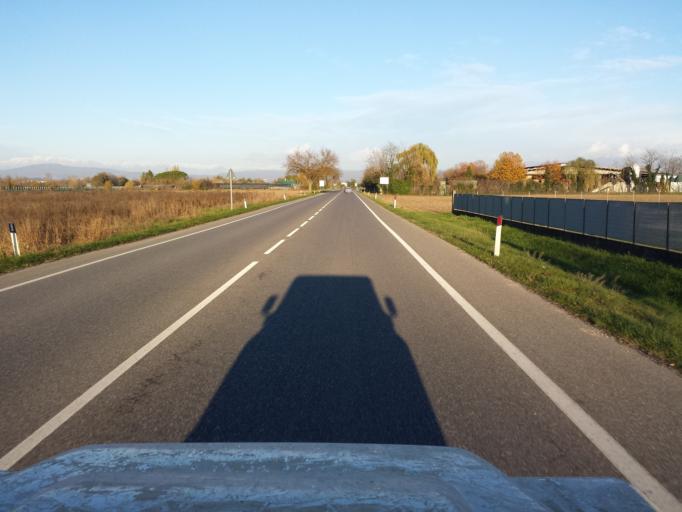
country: IT
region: Friuli Venezia Giulia
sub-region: Provincia di Gorizia
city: Villesse
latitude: 45.8750
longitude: 13.4571
